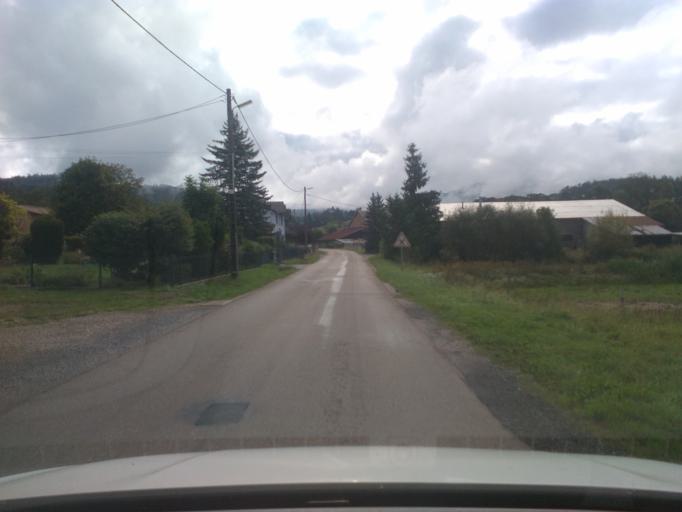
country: FR
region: Lorraine
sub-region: Departement des Vosges
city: Senones
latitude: 48.3444
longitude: 6.9600
